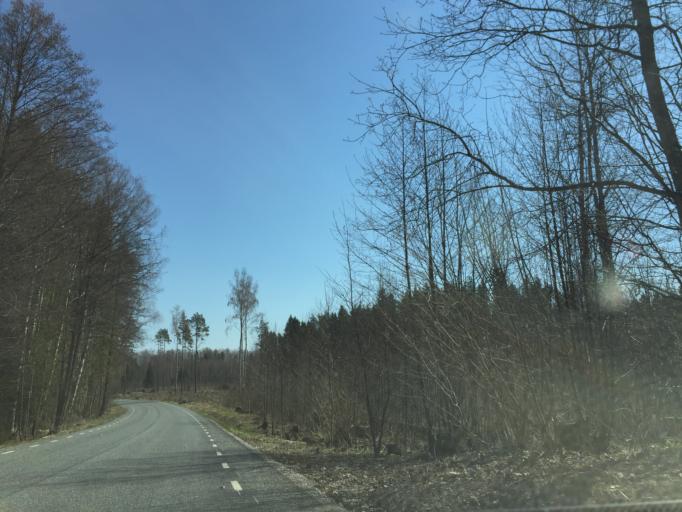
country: EE
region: Tartu
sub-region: Alatskivi vald
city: Kallaste
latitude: 58.5847
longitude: 27.0355
